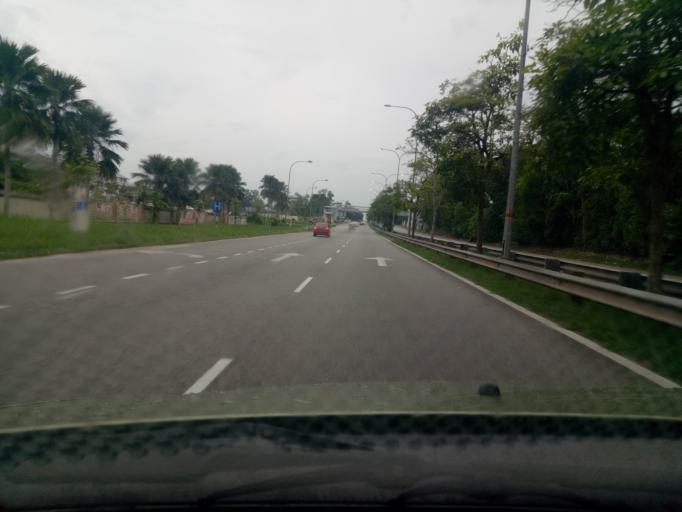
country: MY
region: Kedah
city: Sungai Petani
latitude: 5.6682
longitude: 100.5149
